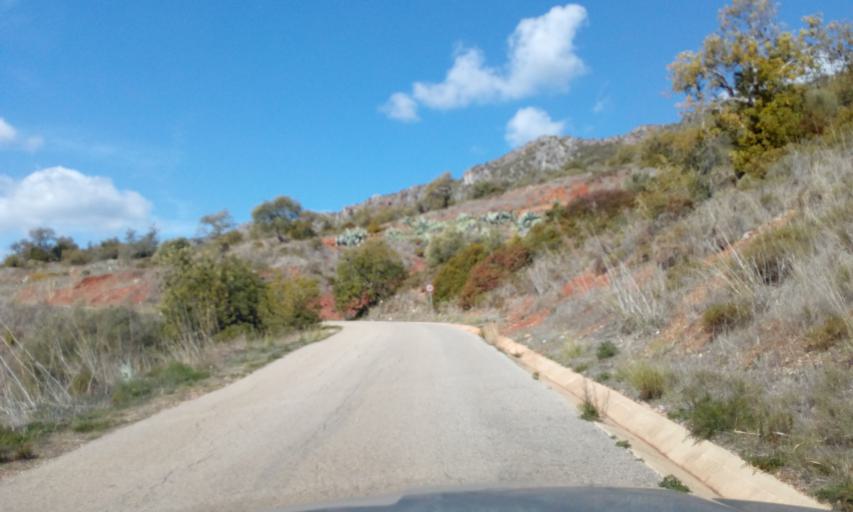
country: PT
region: Faro
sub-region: Loule
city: Boliqueime
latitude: 37.2506
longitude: -8.0960
